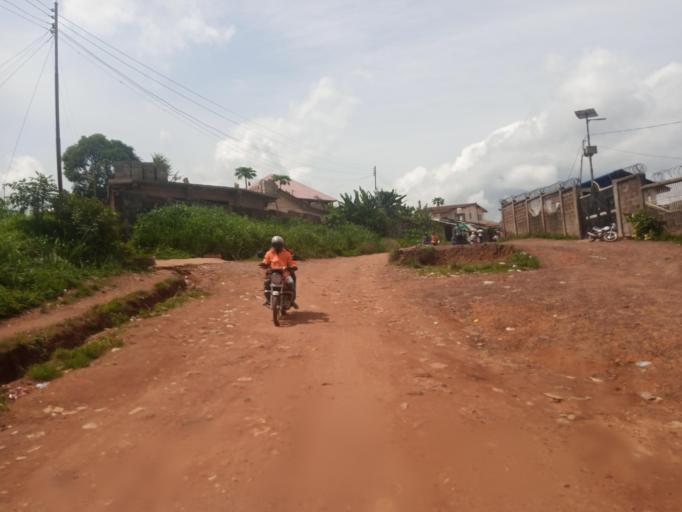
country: SL
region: Southern Province
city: Bo
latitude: 7.9655
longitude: -11.7424
